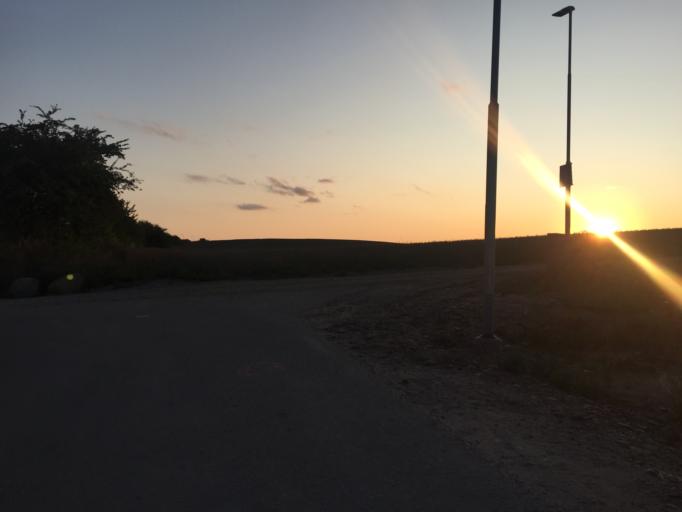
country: SE
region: Skane
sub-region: Svedala Kommun
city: Klagerup
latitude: 55.5977
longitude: 13.2545
